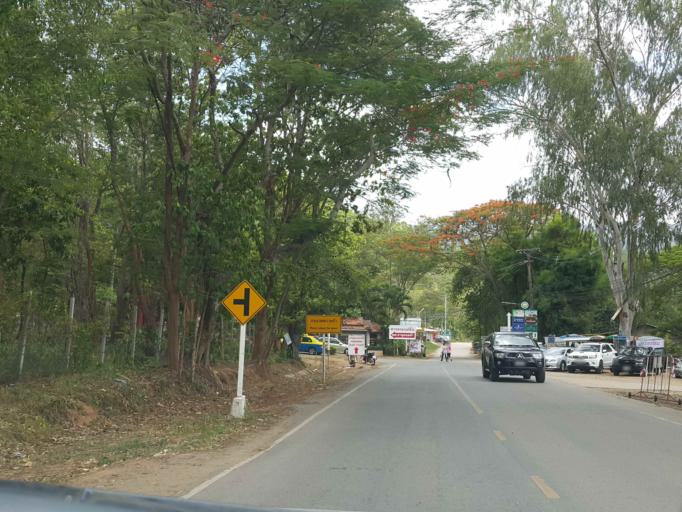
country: TH
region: Chiang Mai
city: Hang Dong
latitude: 18.7560
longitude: 98.9229
